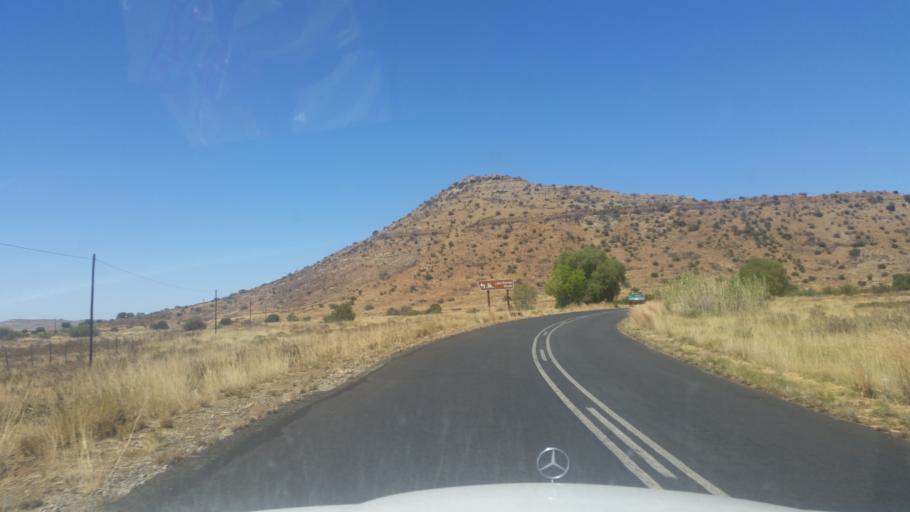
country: ZA
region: Eastern Cape
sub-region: Joe Gqabi District Municipality
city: Burgersdorp
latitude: -30.7427
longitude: 25.7573
